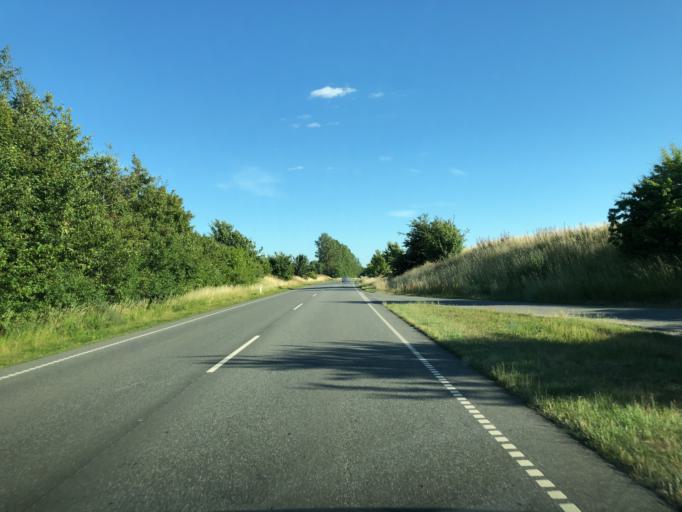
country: DK
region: Central Jutland
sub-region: Arhus Kommune
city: Framlev
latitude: 56.1646
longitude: 10.0057
